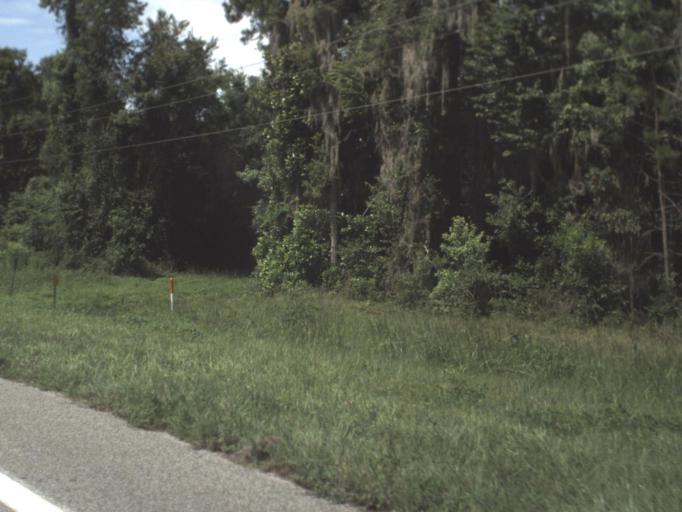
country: US
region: Florida
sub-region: Hamilton County
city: Jasper
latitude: 30.4328
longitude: -82.9338
